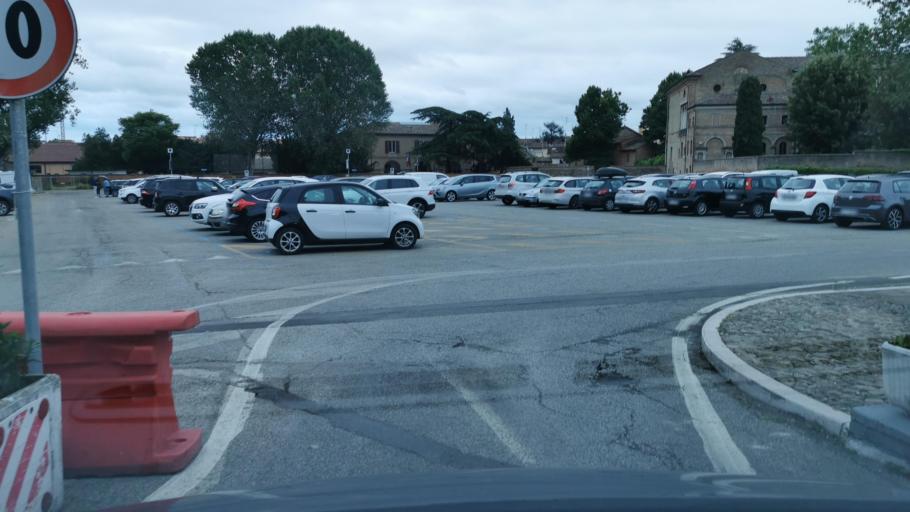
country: IT
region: Emilia-Romagna
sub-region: Provincia di Ravenna
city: Ravenna
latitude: 44.4220
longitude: 12.1955
